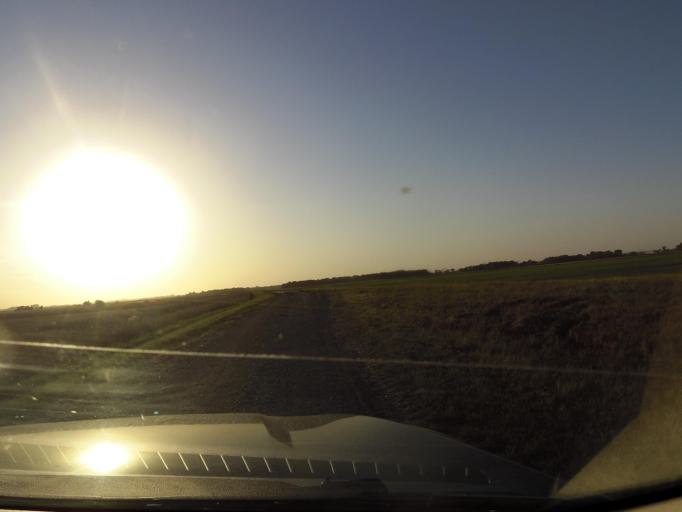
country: US
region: North Dakota
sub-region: Walsh County
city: Grafton
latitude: 48.4195
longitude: -97.4555
